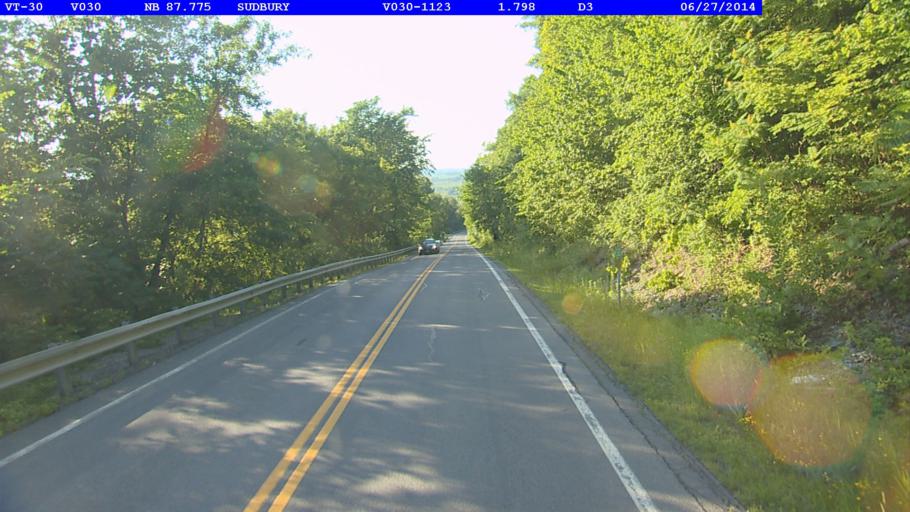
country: US
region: Vermont
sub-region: Rutland County
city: Brandon
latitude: 43.7741
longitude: -73.2023
